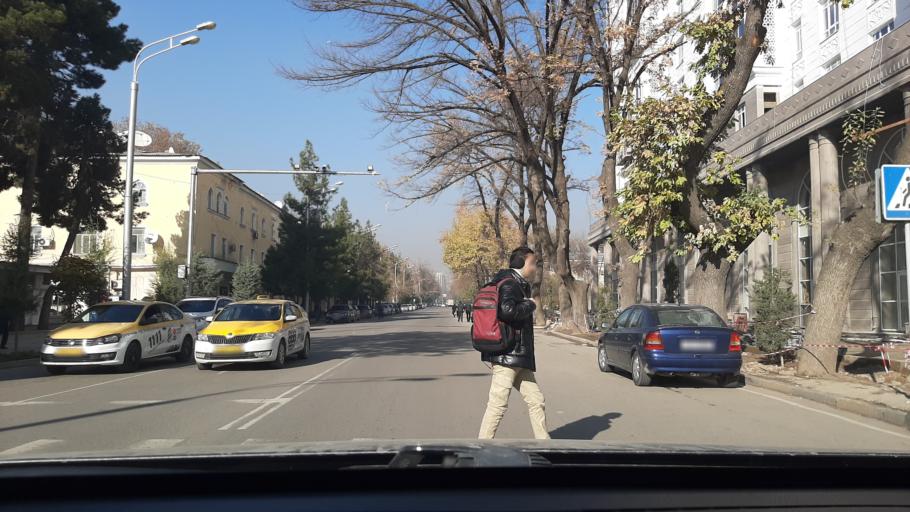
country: TJ
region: Dushanbe
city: Dushanbe
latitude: 38.5633
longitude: 68.7999
